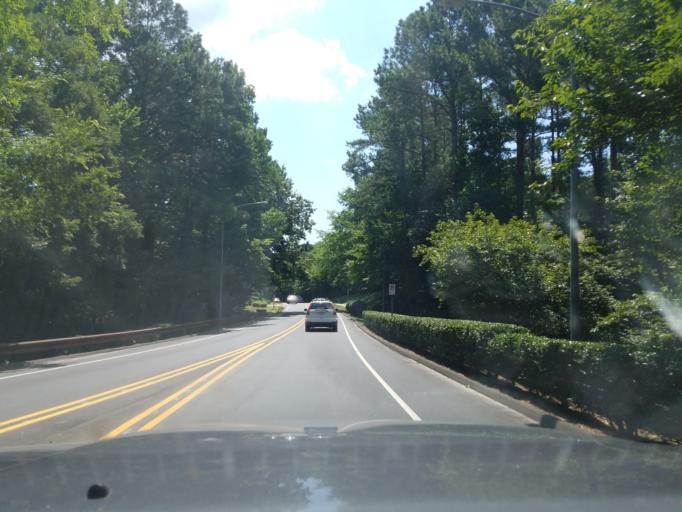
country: US
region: North Carolina
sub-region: Durham County
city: Durham
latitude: 35.9235
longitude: -78.9413
